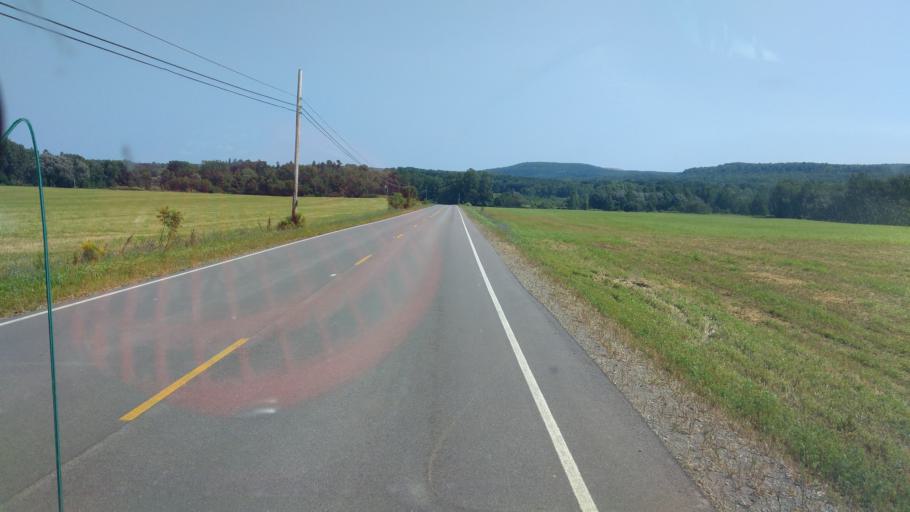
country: US
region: New York
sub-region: Allegany County
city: Belmont
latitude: 42.2579
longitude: -78.0557
